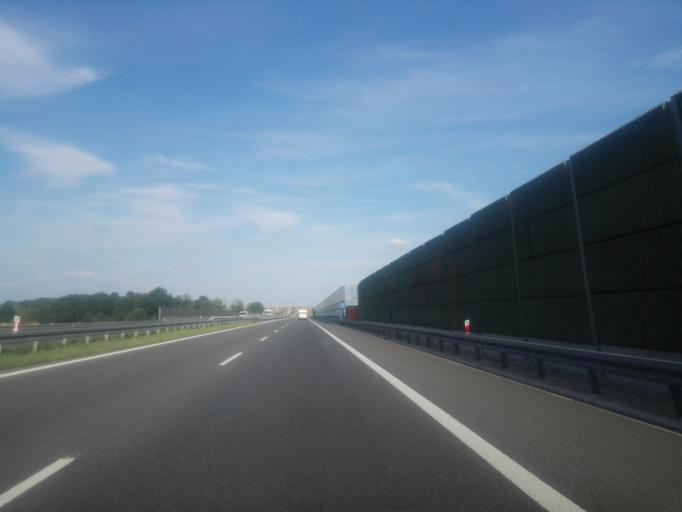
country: PL
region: Lower Silesian Voivodeship
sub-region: Powiat wroclawski
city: Dlugoleka
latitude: 51.2290
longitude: 17.2534
